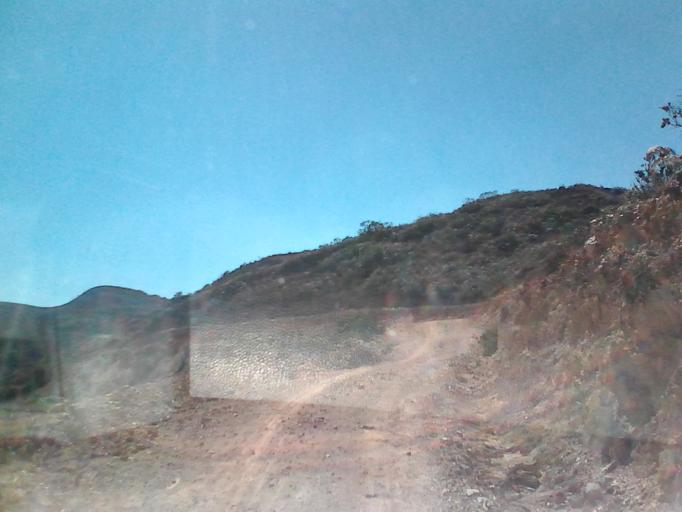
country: CO
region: Boyaca
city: Sachica
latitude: 5.5414
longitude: -73.5564
